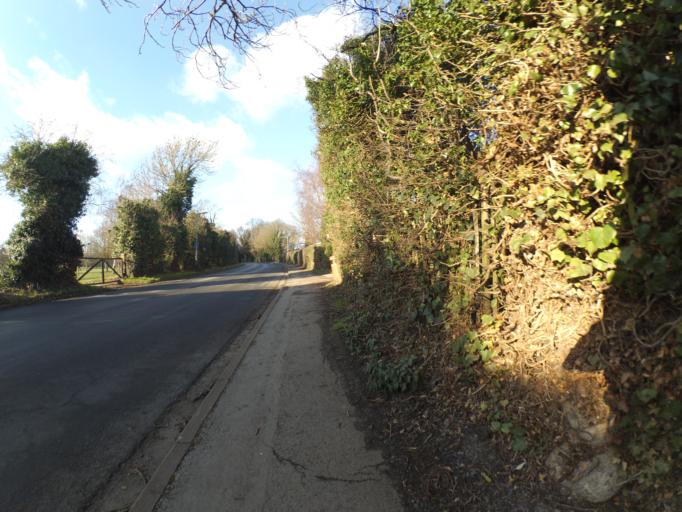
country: GB
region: England
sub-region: Nottinghamshire
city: Gotham
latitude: 52.9159
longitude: -1.2220
